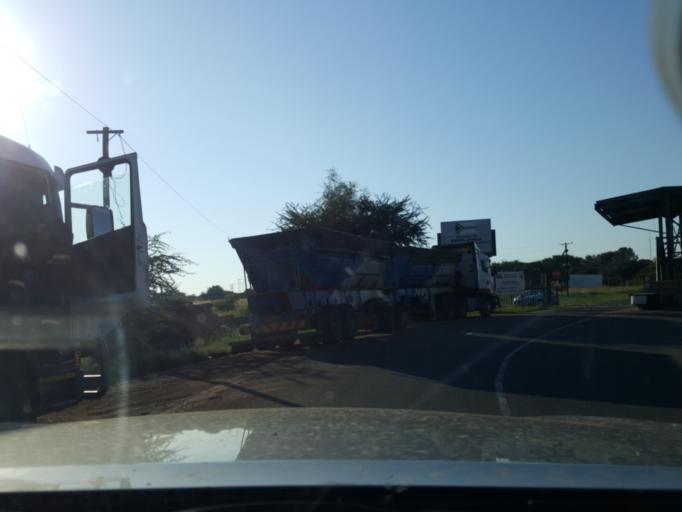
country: ZA
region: North-West
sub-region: Ngaka Modiri Molema District Municipality
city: Mmabatho
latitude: -25.6463
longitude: 25.5752
